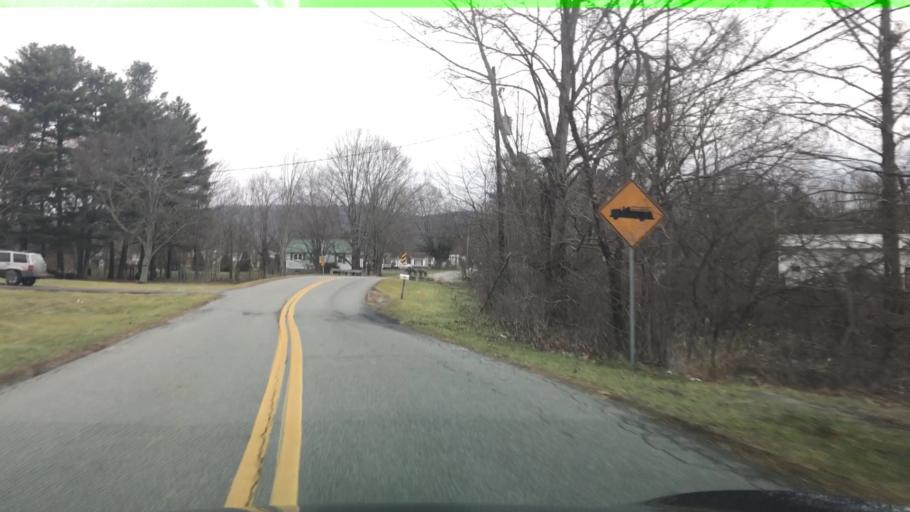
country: US
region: Virginia
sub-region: Smyth County
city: Atkins
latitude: 36.7746
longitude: -81.4116
